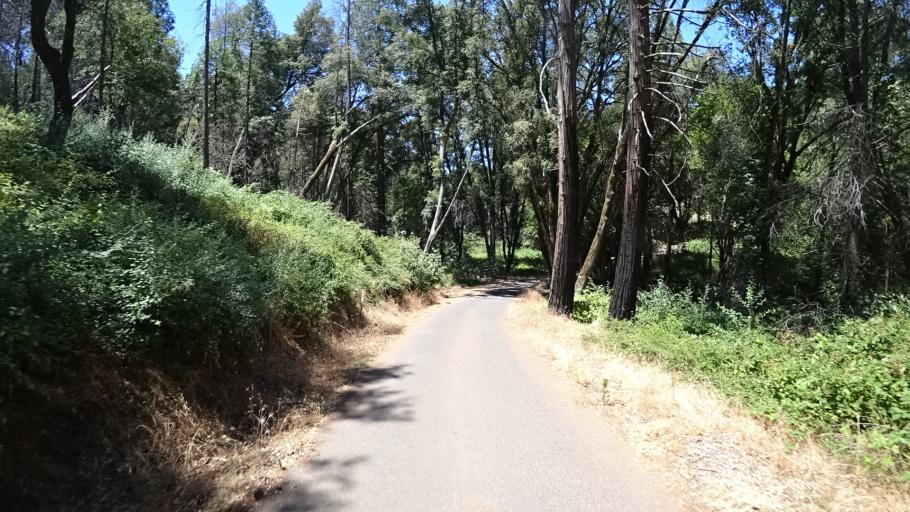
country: US
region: California
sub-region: Calaveras County
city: Mountain Ranch
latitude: 38.2740
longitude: -120.5912
